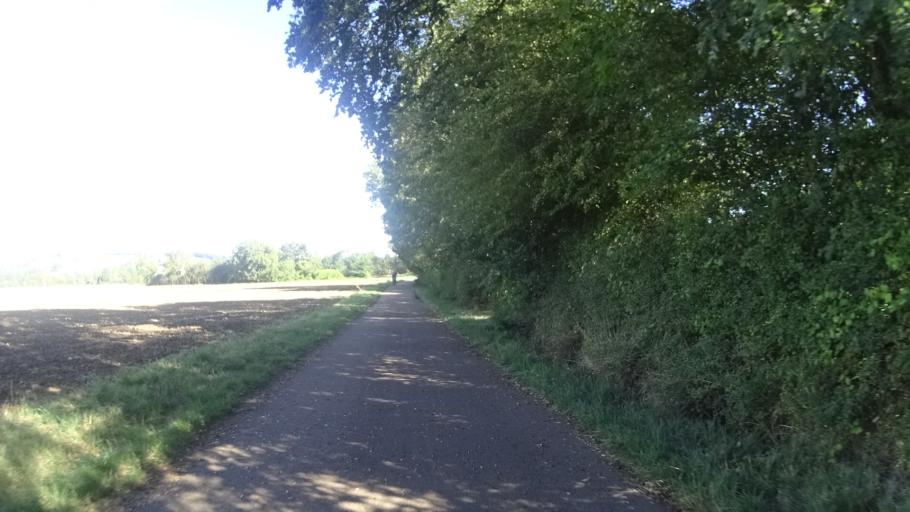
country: FR
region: Centre
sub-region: Departement du Cher
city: Saint-Satur
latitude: 47.3294
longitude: 2.8632
